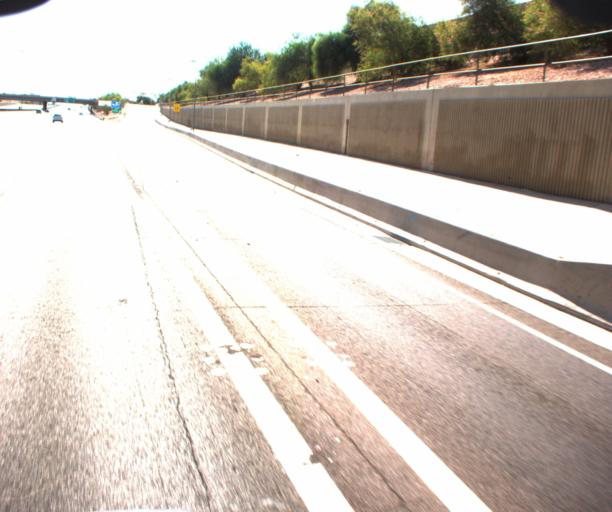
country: US
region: Arizona
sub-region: Maricopa County
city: Guadalupe
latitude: 33.3854
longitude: -111.9435
